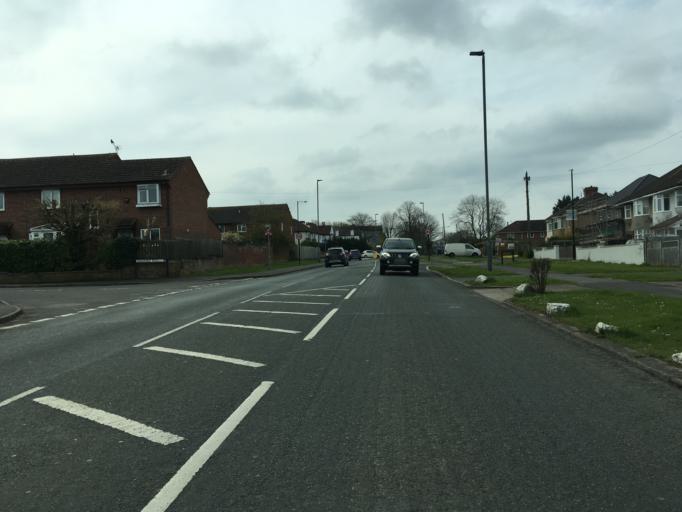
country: GB
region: England
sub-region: South Gloucestershire
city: Almondsbury
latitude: 51.5116
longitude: -2.6000
